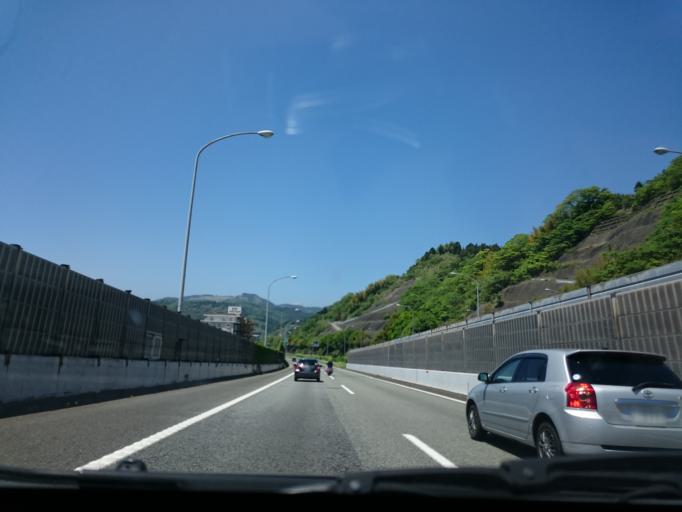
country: JP
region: Kanagawa
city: Odawara
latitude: 35.3576
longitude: 139.1104
